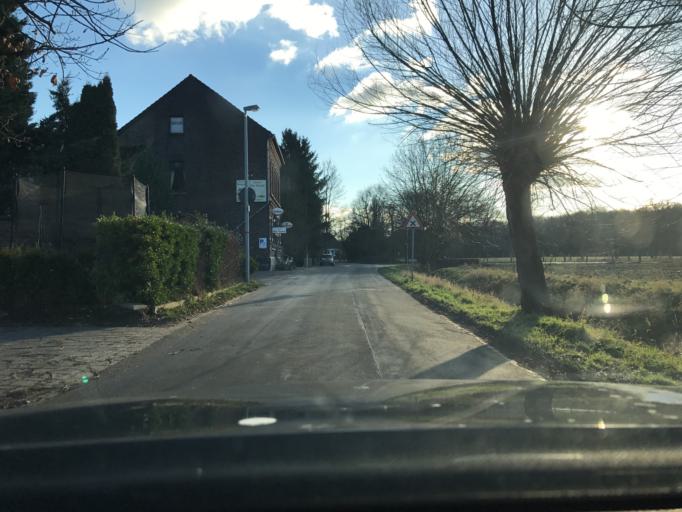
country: DE
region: North Rhine-Westphalia
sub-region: Regierungsbezirk Dusseldorf
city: Krefeld
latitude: 51.3624
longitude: 6.6048
